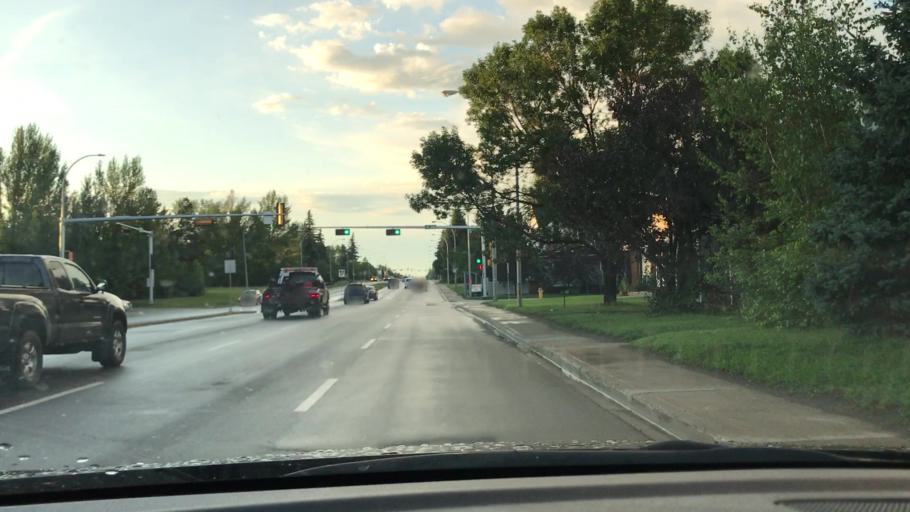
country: CA
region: Alberta
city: Edmonton
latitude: 53.5136
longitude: -113.4428
